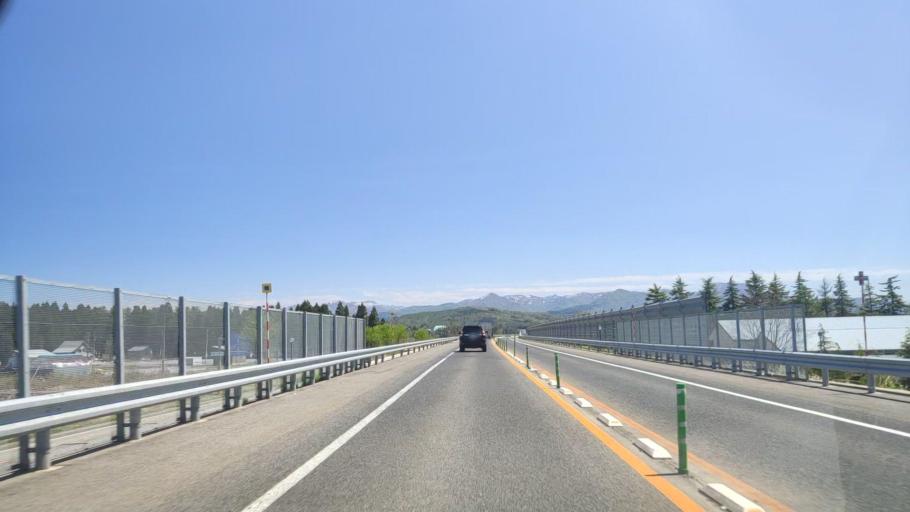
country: JP
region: Yamagata
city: Obanazawa
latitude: 38.6190
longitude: 140.3835
